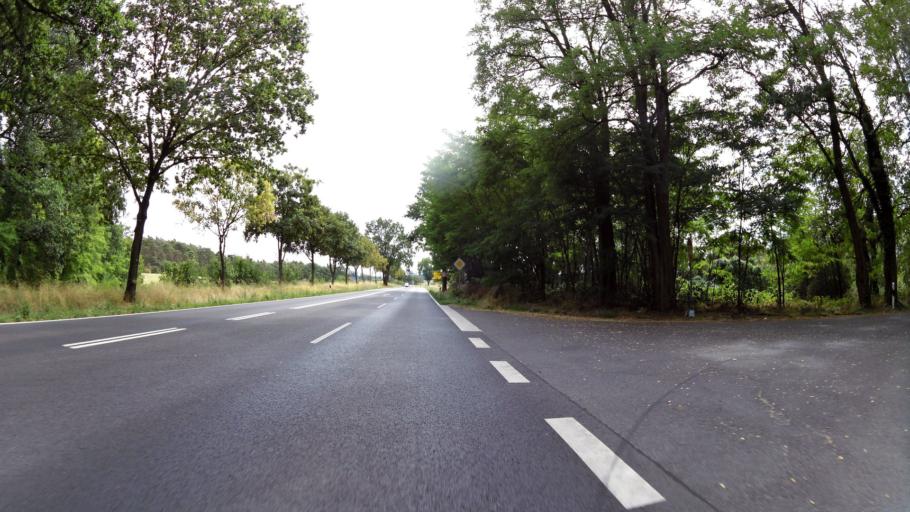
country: DE
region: Brandenburg
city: Neuzelle
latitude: 52.0807
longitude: 14.6588
